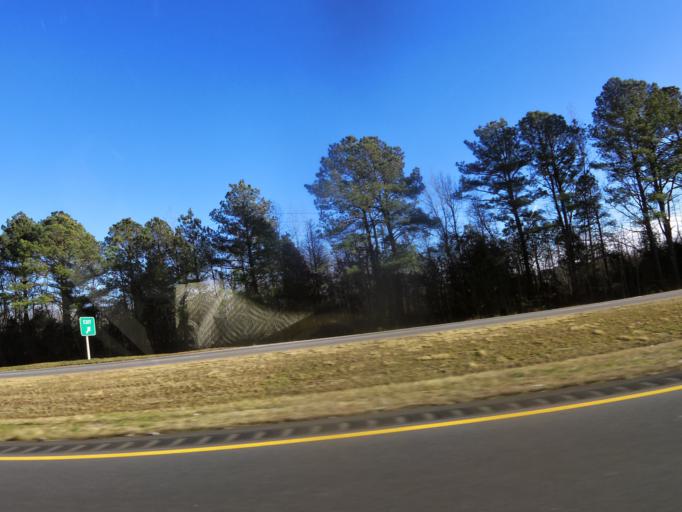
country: US
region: Virginia
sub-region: City of Suffolk
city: Suffolk
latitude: 36.7432
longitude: -76.6162
